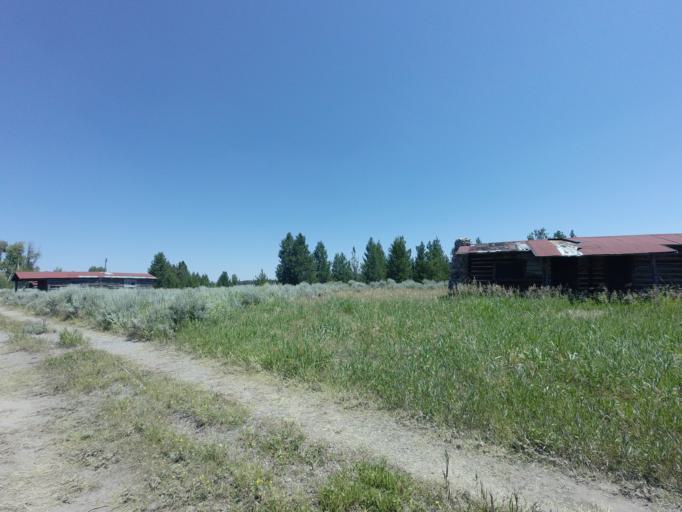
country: US
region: Wyoming
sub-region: Teton County
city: Jackson
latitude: 43.6947
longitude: -110.6951
